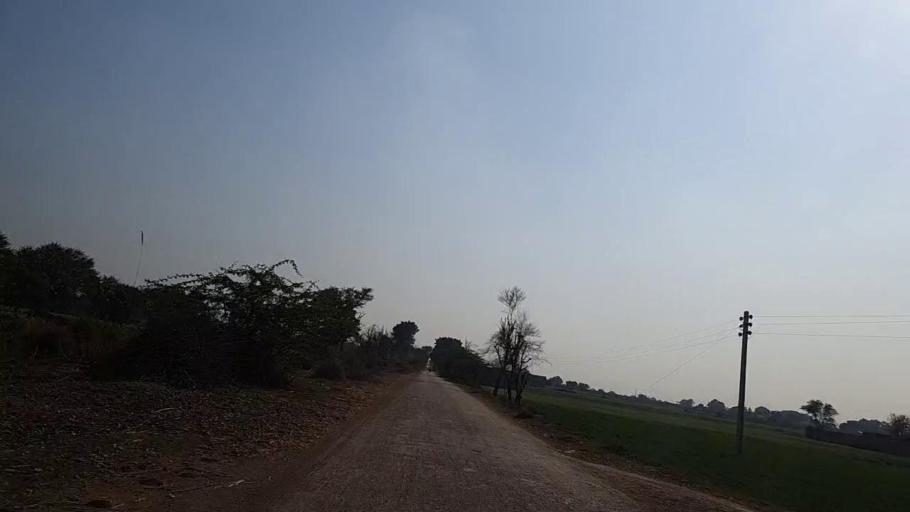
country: PK
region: Sindh
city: Sakrand
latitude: 26.0765
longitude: 68.2899
